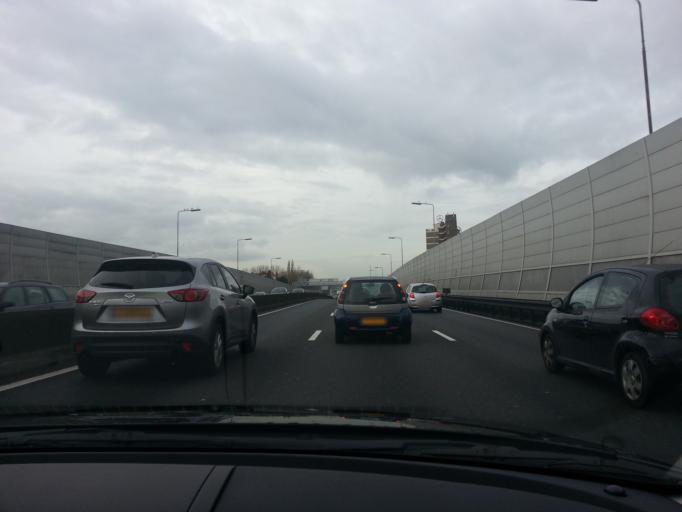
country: NL
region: South Holland
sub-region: Gemeente Schiedam
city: Schiedam
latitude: 51.9425
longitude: 4.4256
